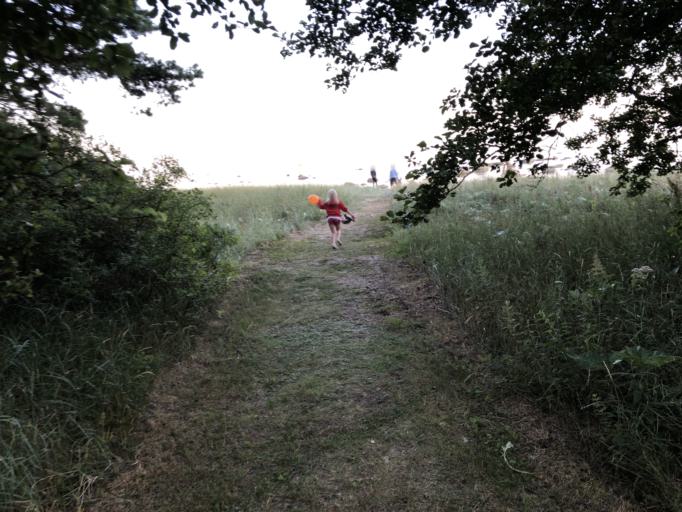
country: EE
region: Hiiumaa
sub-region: Kaerdla linn
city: Kardla
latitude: 58.8838
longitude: 22.2518
